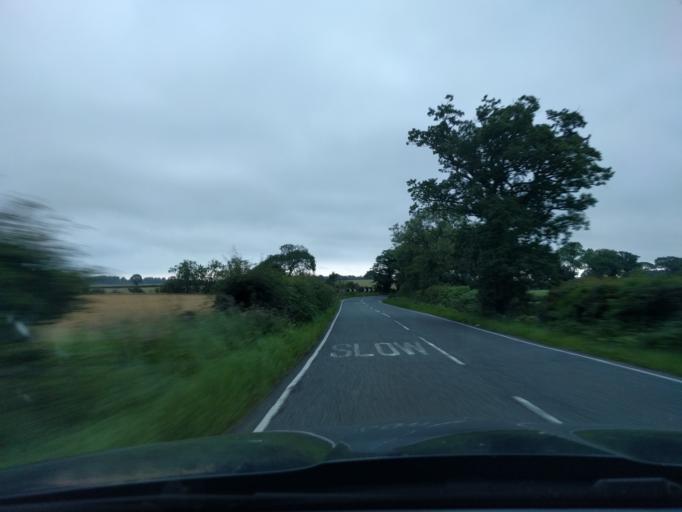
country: GB
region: England
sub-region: Northumberland
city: Felton
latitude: 55.2562
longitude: -1.6708
